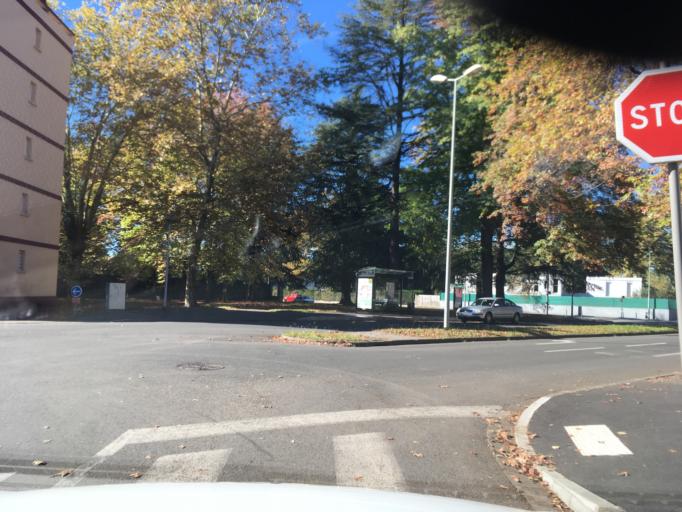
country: FR
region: Aquitaine
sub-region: Departement des Pyrenees-Atlantiques
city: Pau
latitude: 43.3093
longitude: -0.3692
